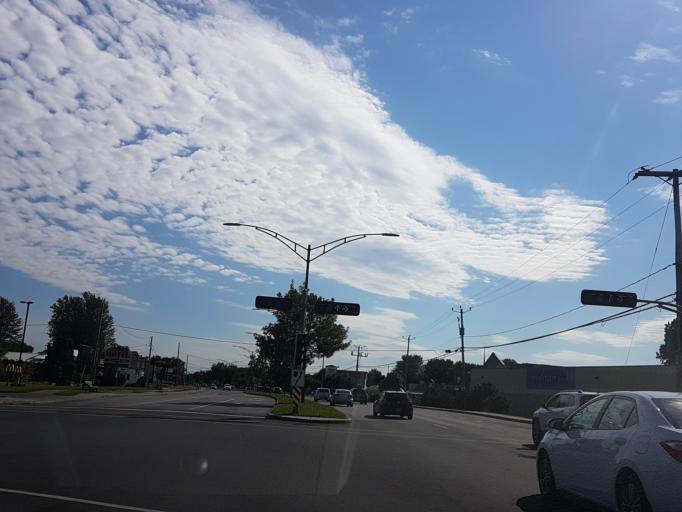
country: CA
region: Quebec
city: Sainte-Catherine
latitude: 46.3244
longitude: -72.5645
